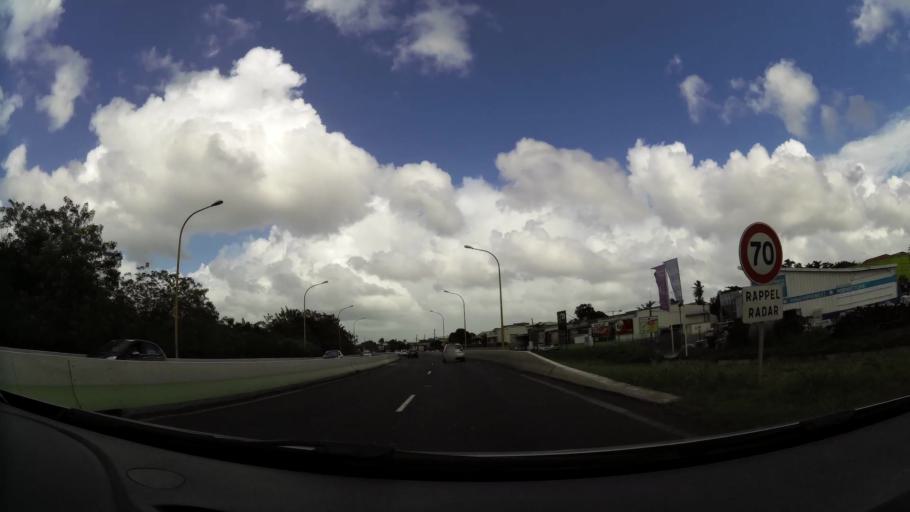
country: MQ
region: Martinique
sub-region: Martinique
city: Ducos
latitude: 14.5269
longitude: -60.9821
